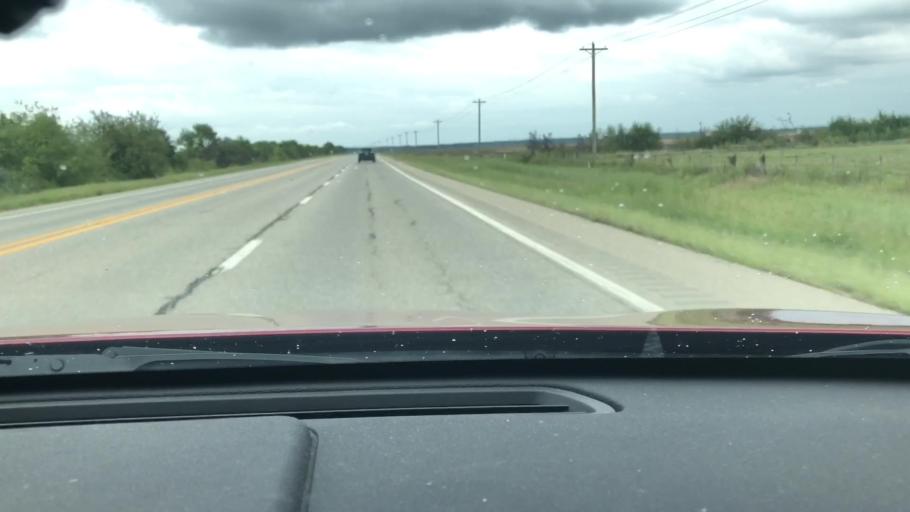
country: US
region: Arkansas
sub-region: Lafayette County
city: Lewisville
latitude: 33.4124
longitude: -93.7883
